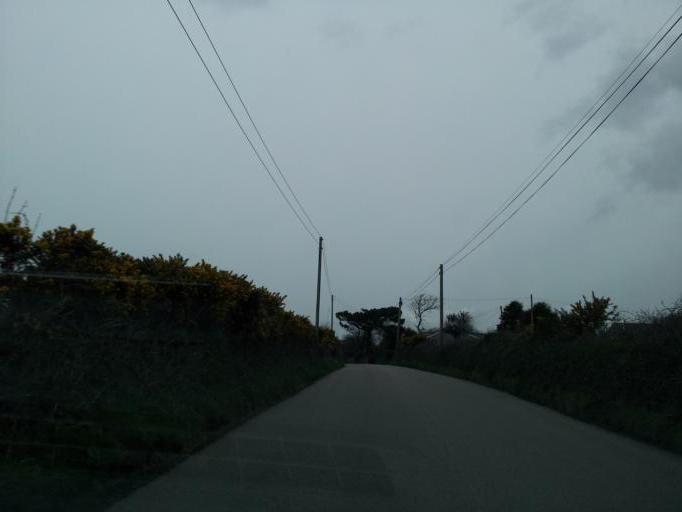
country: GB
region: England
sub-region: Cornwall
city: St. Day
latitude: 50.2610
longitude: -5.1942
